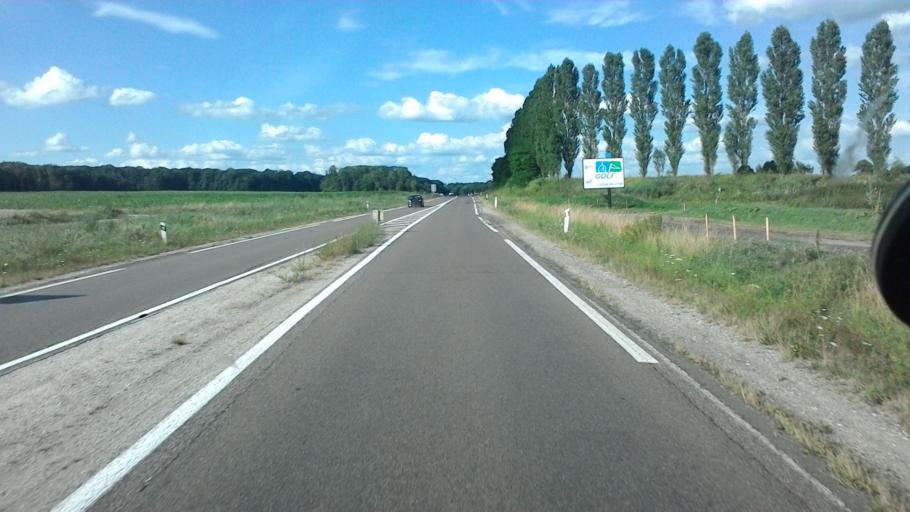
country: FR
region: Franche-Comte
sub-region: Departement de la Haute-Saone
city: Luxeuil-les-Bains
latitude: 47.7331
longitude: 6.3151
